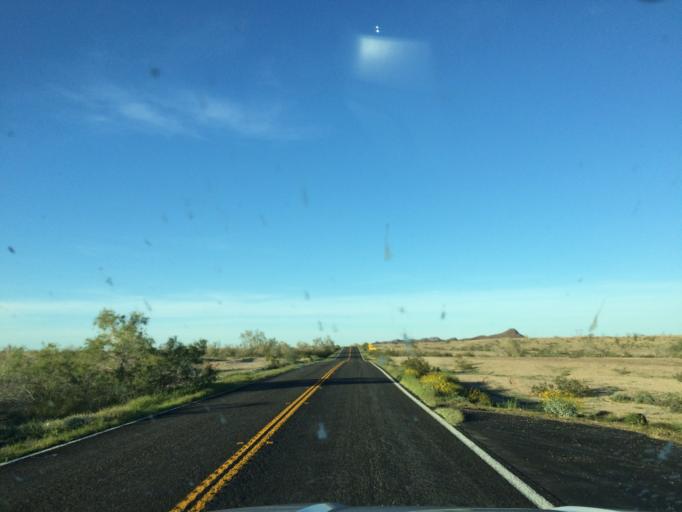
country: MX
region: Baja California
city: Los Algodones
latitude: 33.1183
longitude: -114.8883
